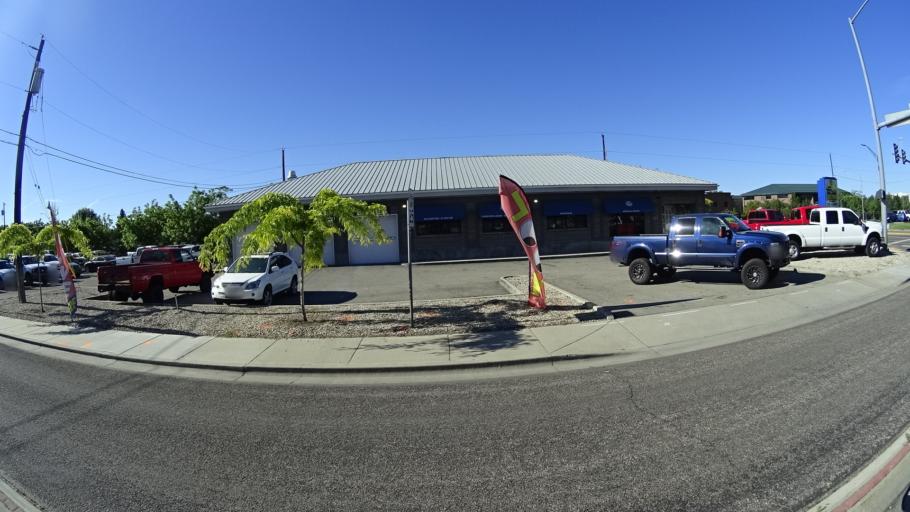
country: US
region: Idaho
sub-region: Ada County
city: Garden City
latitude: 43.6189
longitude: -116.2429
